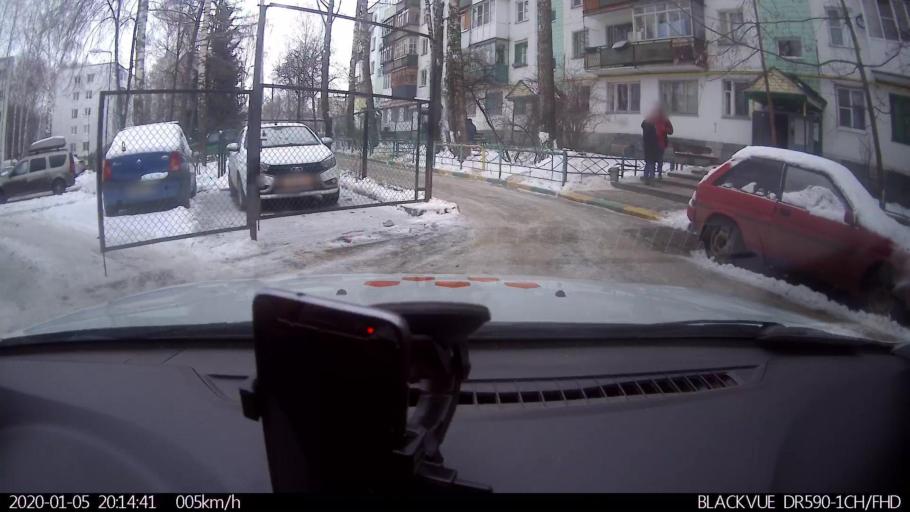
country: RU
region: Nizjnij Novgorod
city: Afonino
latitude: 56.2878
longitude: 44.0471
